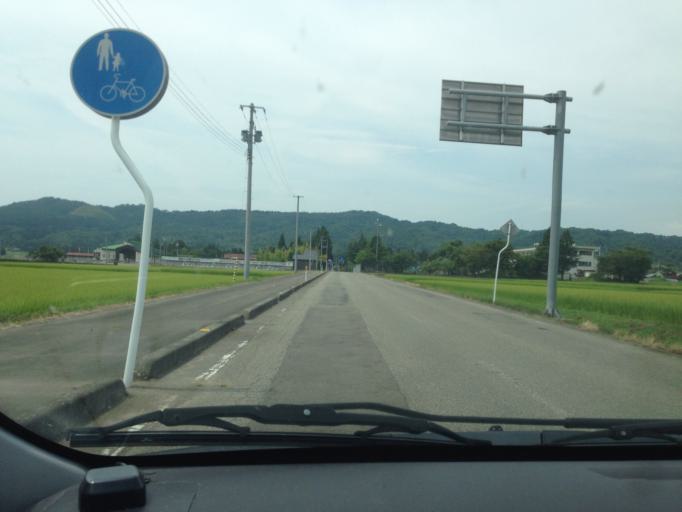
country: JP
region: Fukushima
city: Kitakata
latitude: 37.7077
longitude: 139.8601
